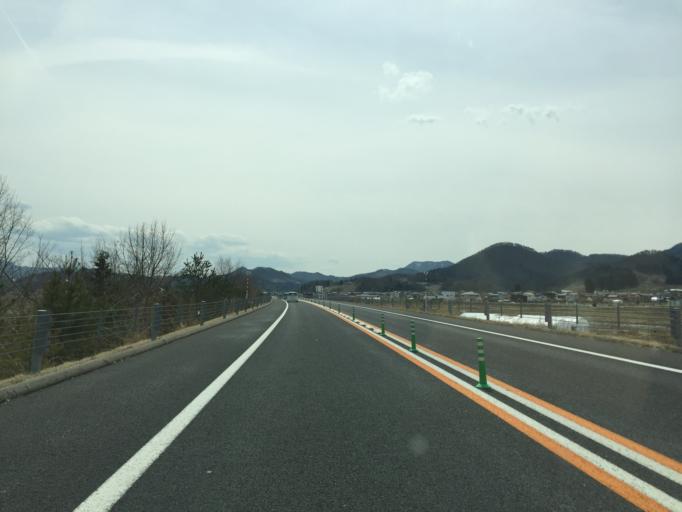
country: JP
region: Yamagata
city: Kaminoyama
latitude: 38.2394
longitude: 140.2754
